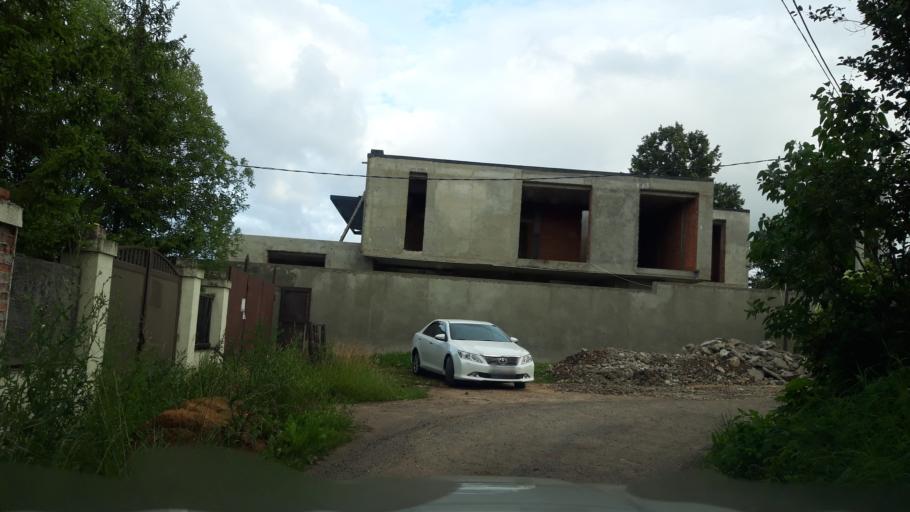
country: RU
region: Moskovskaya
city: Solnechnogorsk
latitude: 56.1050
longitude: 36.8125
